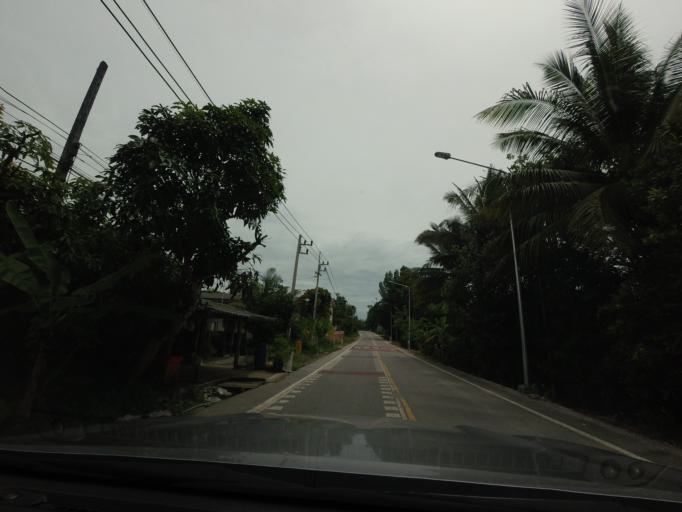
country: TH
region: Pattani
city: Kapho
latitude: 6.5824
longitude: 101.5348
